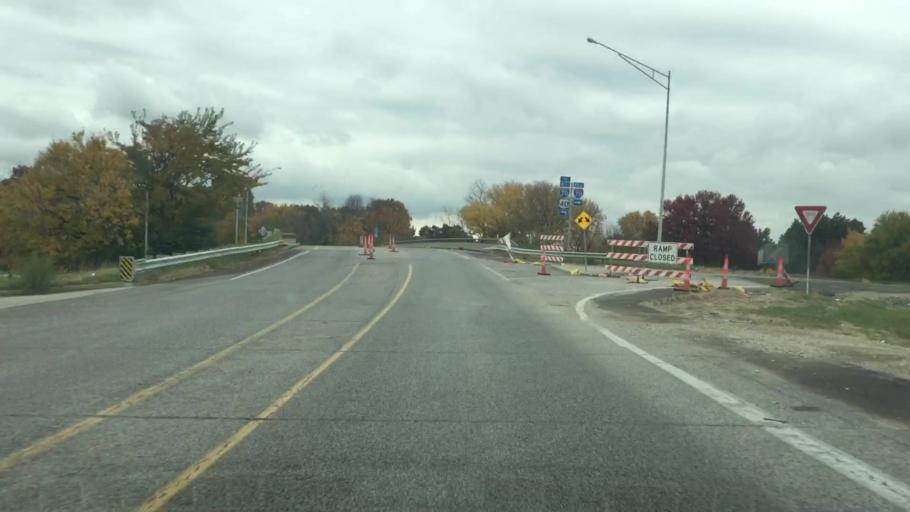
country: US
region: Missouri
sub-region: Jackson County
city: Raytown
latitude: 39.0462
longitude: -94.4392
